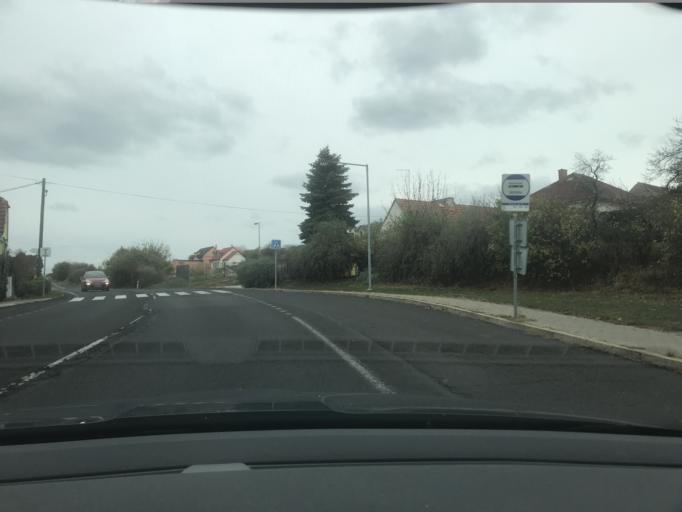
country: CZ
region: Ustecky
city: Cizkovice
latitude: 50.4893
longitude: 14.0213
